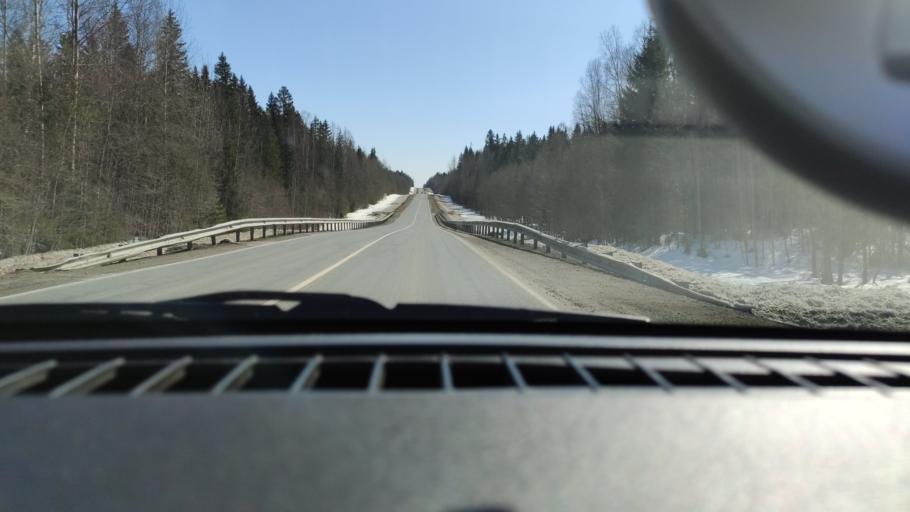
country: RU
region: Perm
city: Perm
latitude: 58.1633
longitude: 56.2427
